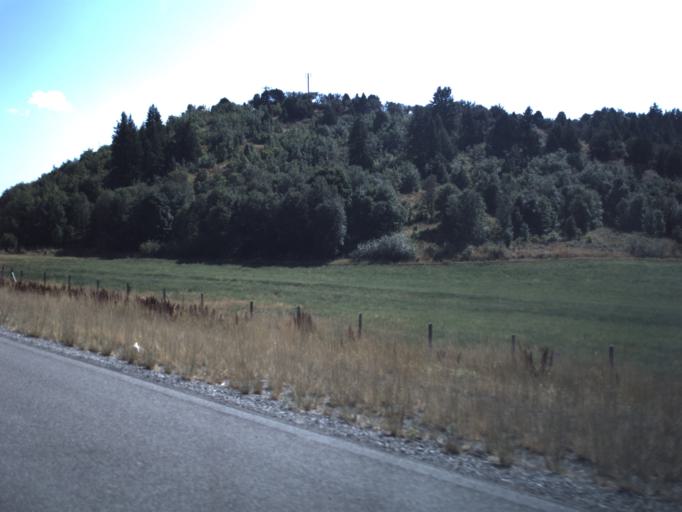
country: US
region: Utah
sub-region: Box Elder County
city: Brigham City
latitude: 41.5528
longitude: -111.9550
